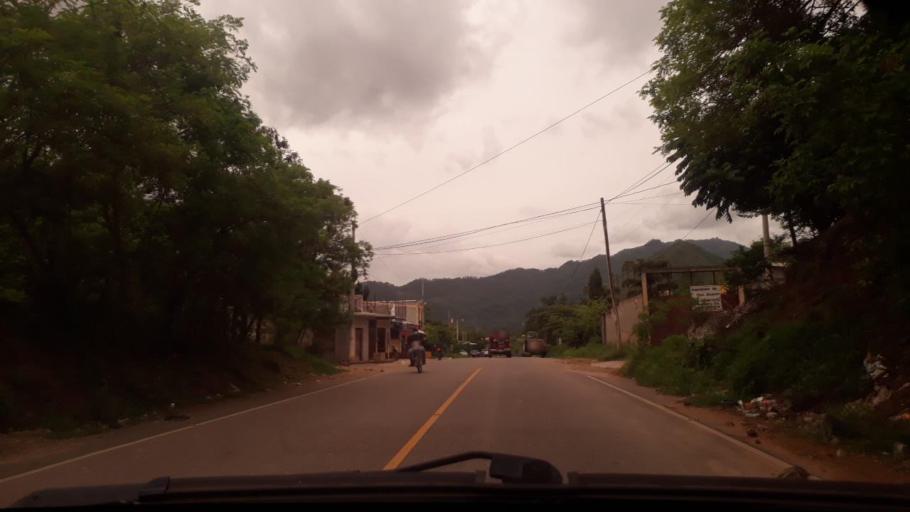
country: GT
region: Chiquimula
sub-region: Municipio de Camotan
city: Camotan
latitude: 14.8177
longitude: -89.3720
